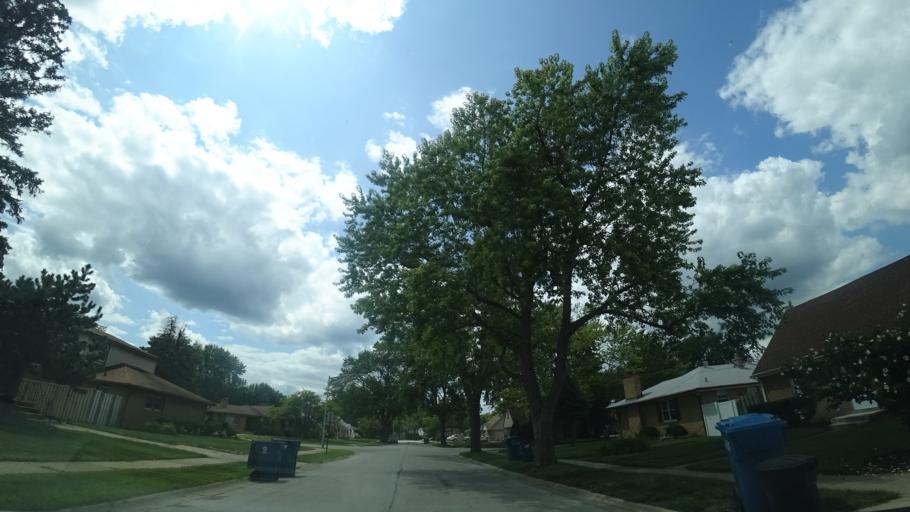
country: US
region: Illinois
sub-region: Cook County
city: Alsip
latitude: 41.6805
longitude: -87.7331
